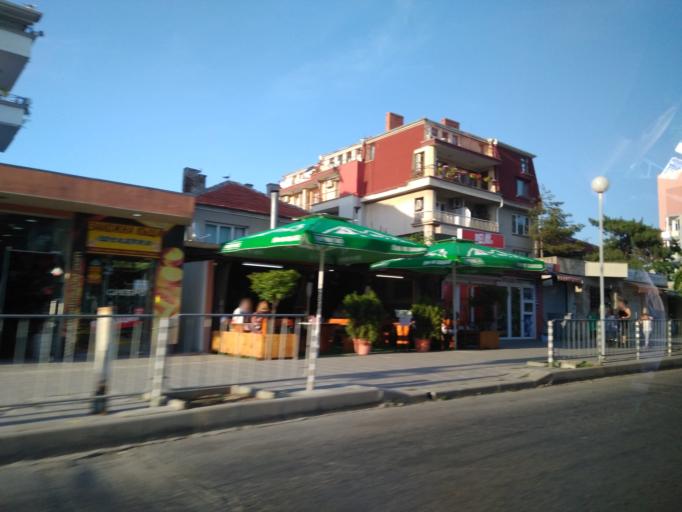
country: BG
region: Burgas
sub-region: Obshtina Nesebur
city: Nesebar
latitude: 42.6625
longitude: 27.7194
